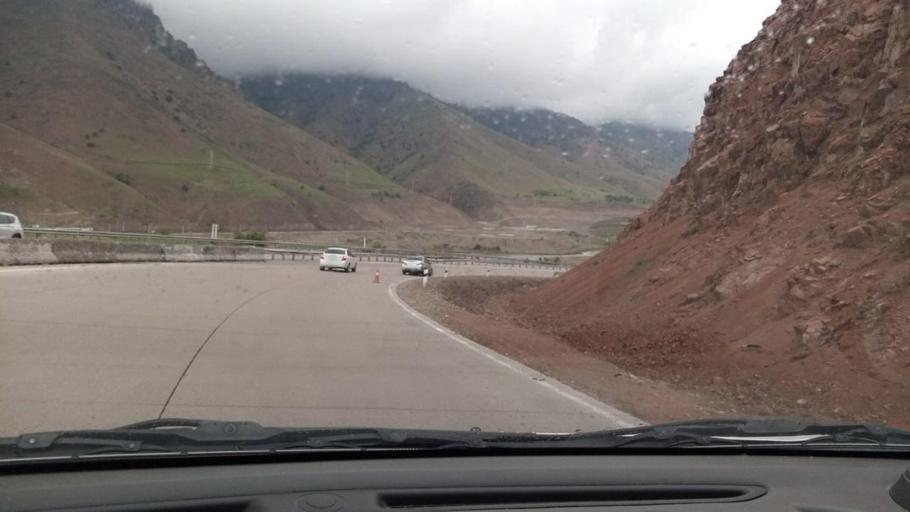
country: UZ
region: Toshkent
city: Angren
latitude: 41.1525
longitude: 70.4446
